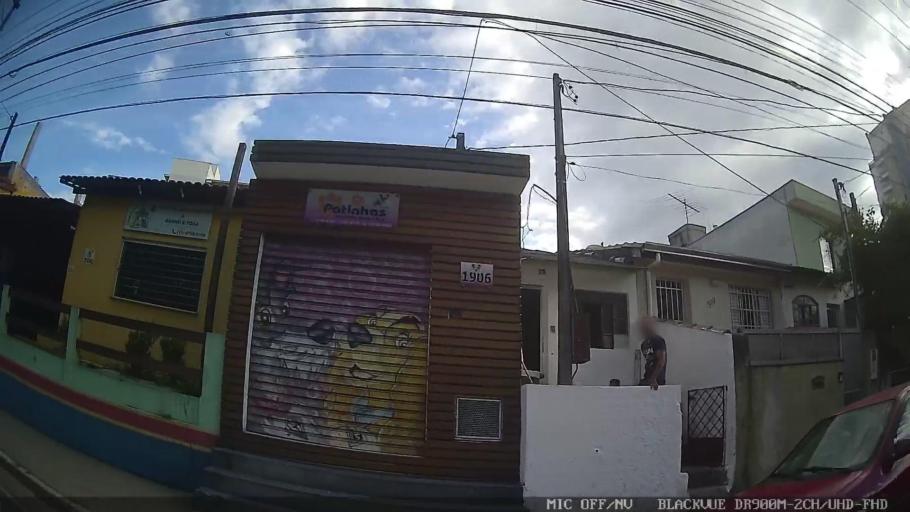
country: BR
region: Sao Paulo
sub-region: Mogi das Cruzes
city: Mogi das Cruzes
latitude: -23.5169
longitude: -46.1752
